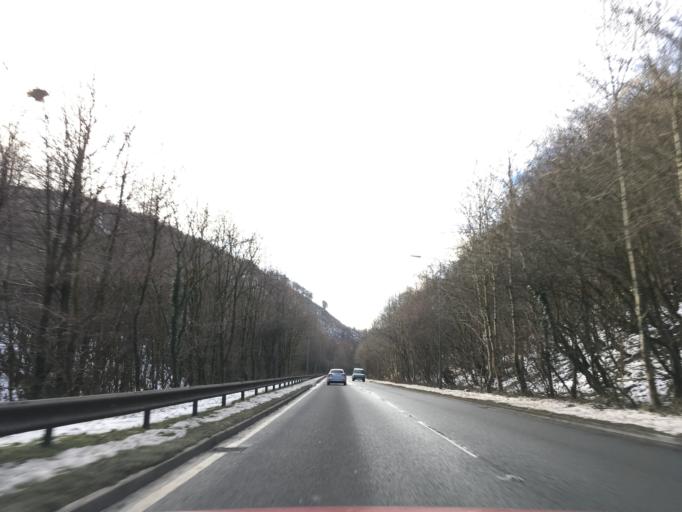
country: GB
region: Wales
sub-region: Torfaen County Borough
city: Pontypool
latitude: 51.6907
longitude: -3.0796
